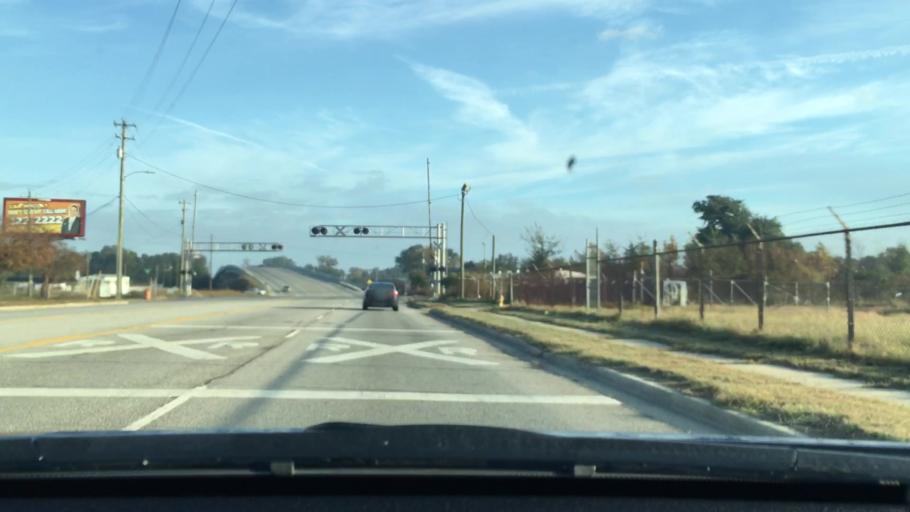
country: US
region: South Carolina
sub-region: Sumter County
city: Sumter
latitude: 33.9127
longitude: -80.3372
